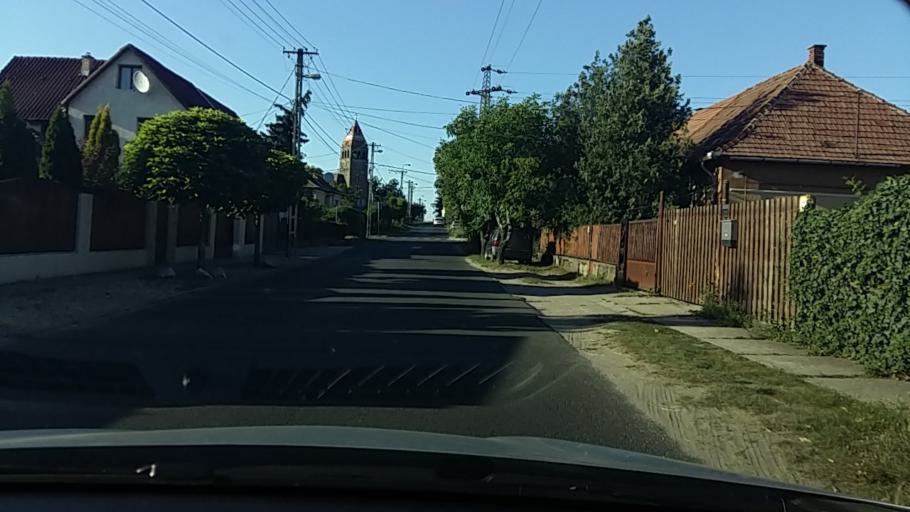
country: HU
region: Pest
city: Dunakeszi
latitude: 47.6304
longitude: 19.1484
